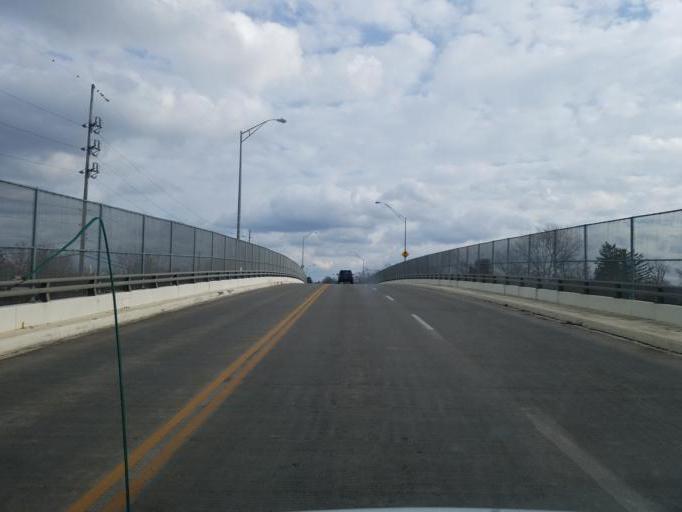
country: US
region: Ohio
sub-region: Marion County
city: Marion
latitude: 40.5843
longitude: -83.1413
